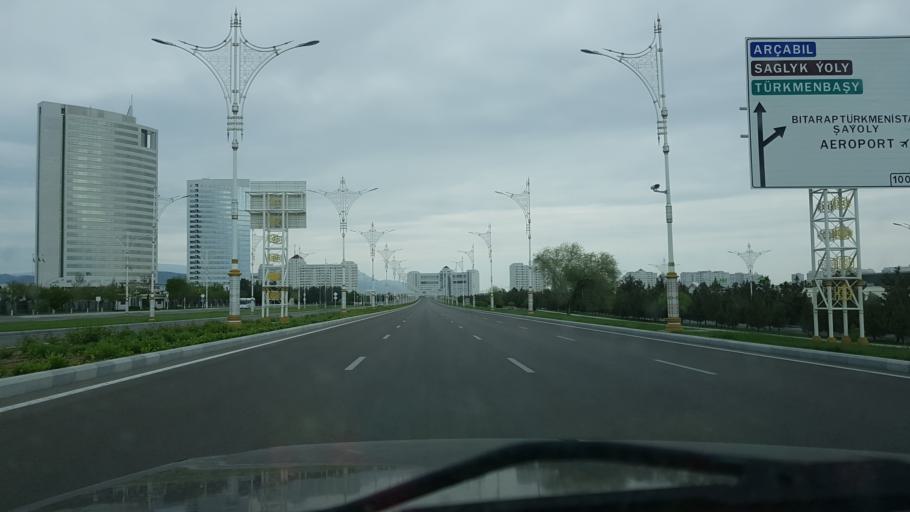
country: TM
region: Ahal
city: Ashgabat
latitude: 37.8895
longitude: 58.3488
